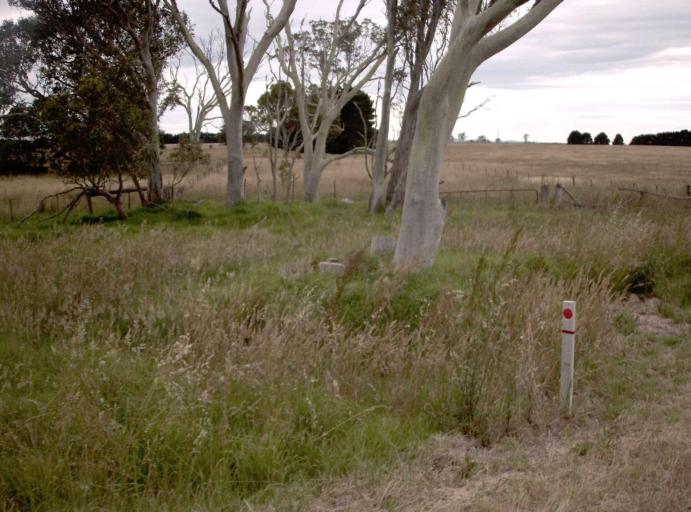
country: AU
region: Victoria
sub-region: East Gippsland
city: Bairnsdale
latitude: -37.9682
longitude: 147.4798
